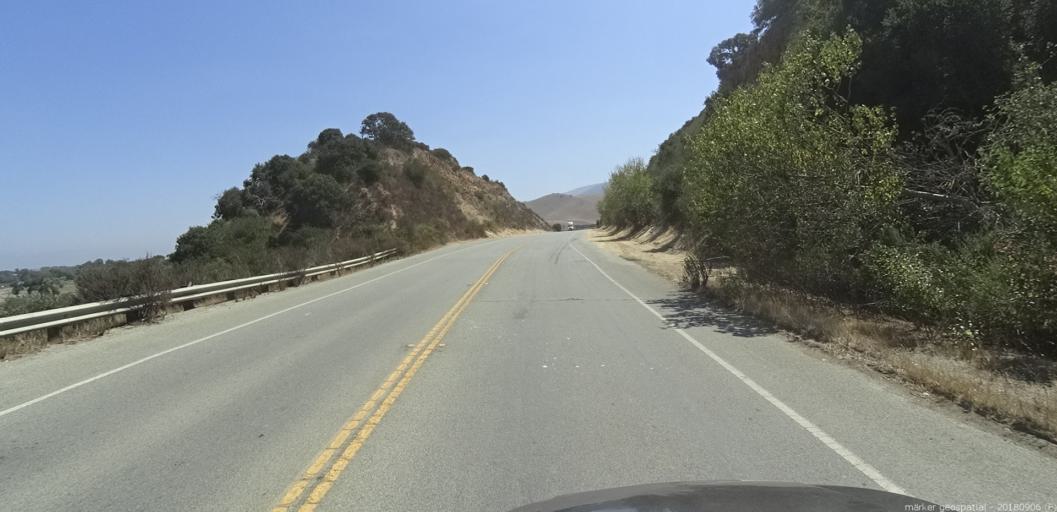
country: US
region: California
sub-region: Monterey County
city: Salinas
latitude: 36.6307
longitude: -121.6924
